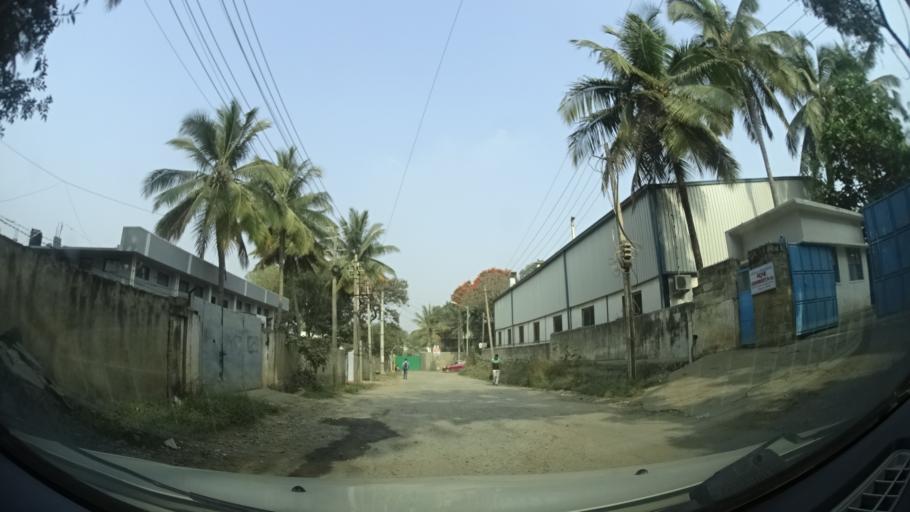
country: IN
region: Karnataka
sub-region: Bangalore Urban
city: Anekal
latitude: 12.8196
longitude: 77.6738
